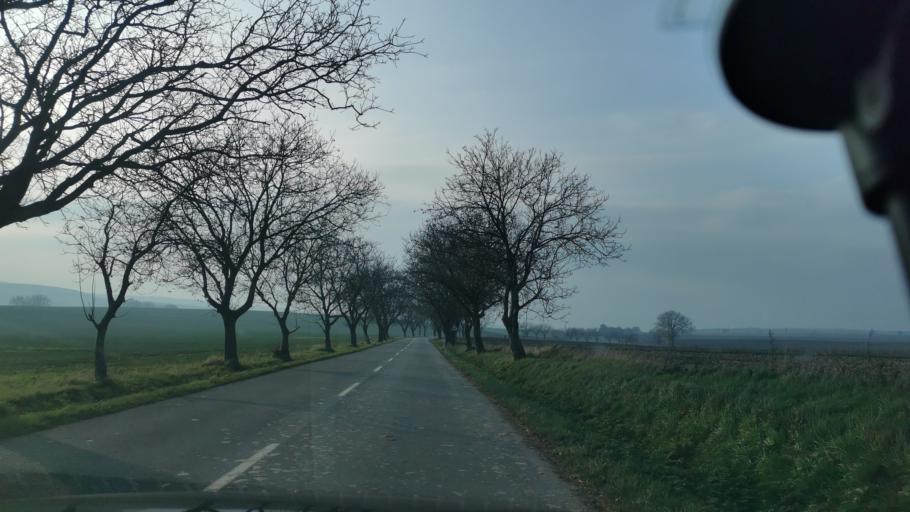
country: CZ
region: South Moravian
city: Sudomerice
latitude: 48.7708
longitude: 17.3063
